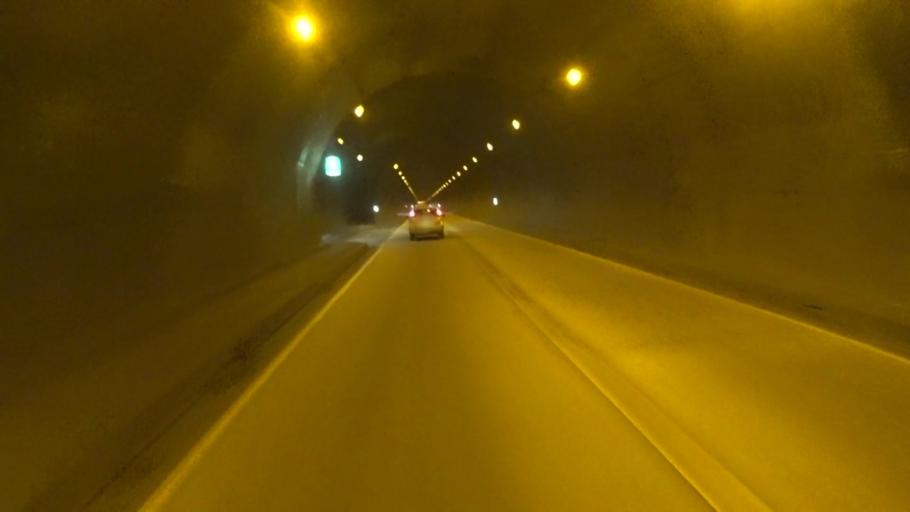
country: JP
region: Kyoto
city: Miyazu
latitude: 35.5481
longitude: 135.1794
